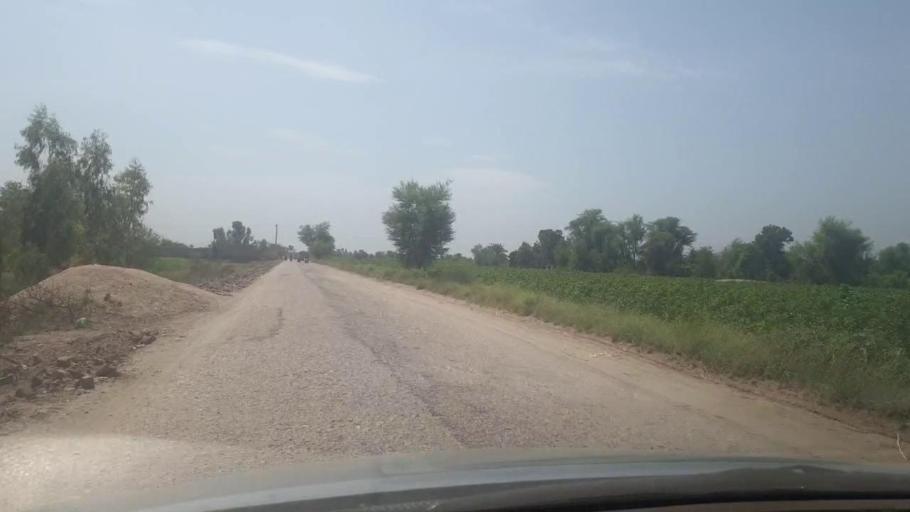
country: PK
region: Sindh
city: Bozdar
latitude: 27.2188
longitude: 68.5686
